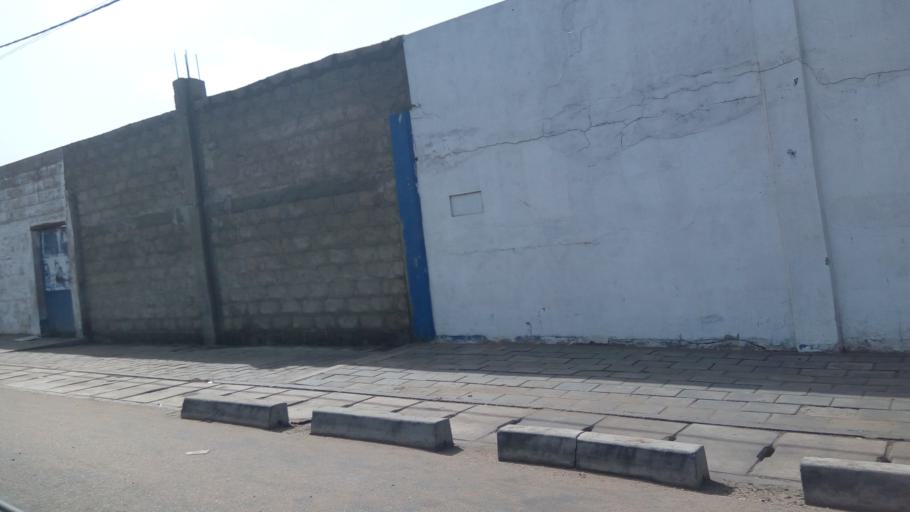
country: TG
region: Maritime
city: Lome
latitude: 6.1510
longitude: 1.2857
